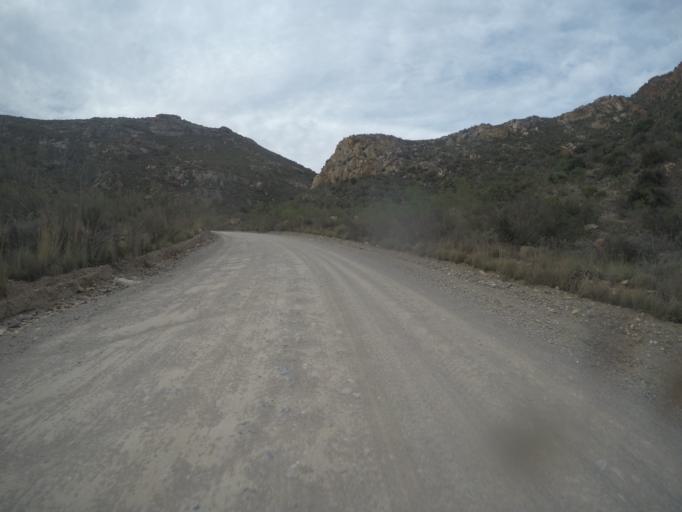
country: ZA
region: Eastern Cape
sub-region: Cacadu District Municipality
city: Willowmore
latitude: -33.5076
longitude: 23.6378
